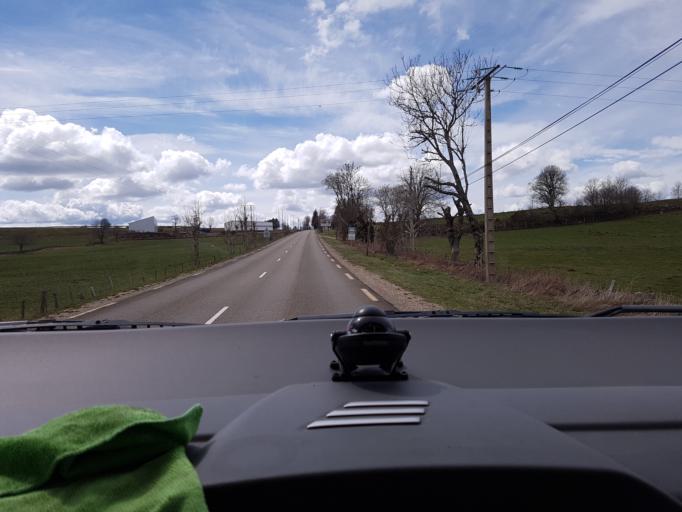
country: FR
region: Midi-Pyrenees
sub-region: Departement de l'Aveyron
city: Laguiole
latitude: 44.7738
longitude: 2.8926
